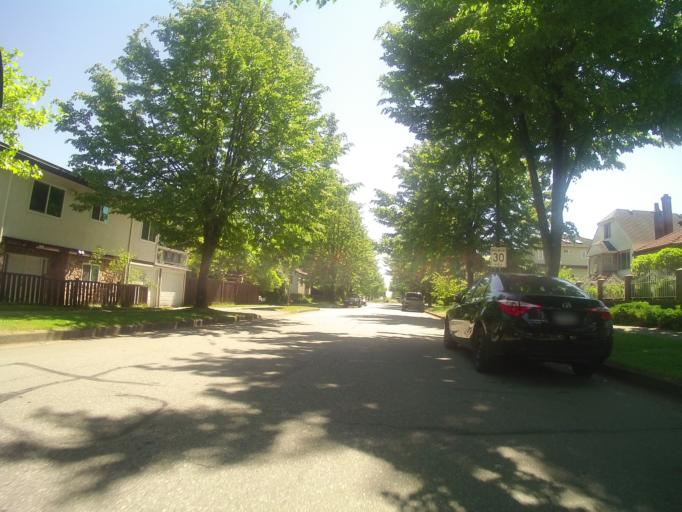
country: CA
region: British Columbia
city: Vancouver
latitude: 49.2353
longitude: -123.1056
